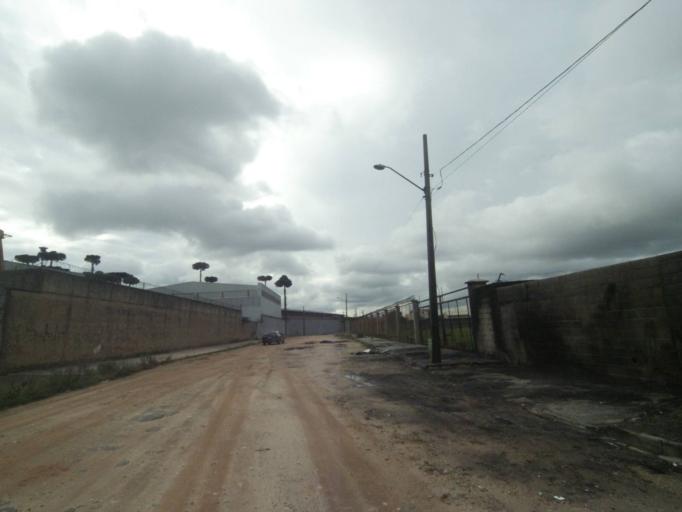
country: BR
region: Parana
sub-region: Curitiba
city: Curitiba
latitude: -25.4862
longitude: -49.3141
